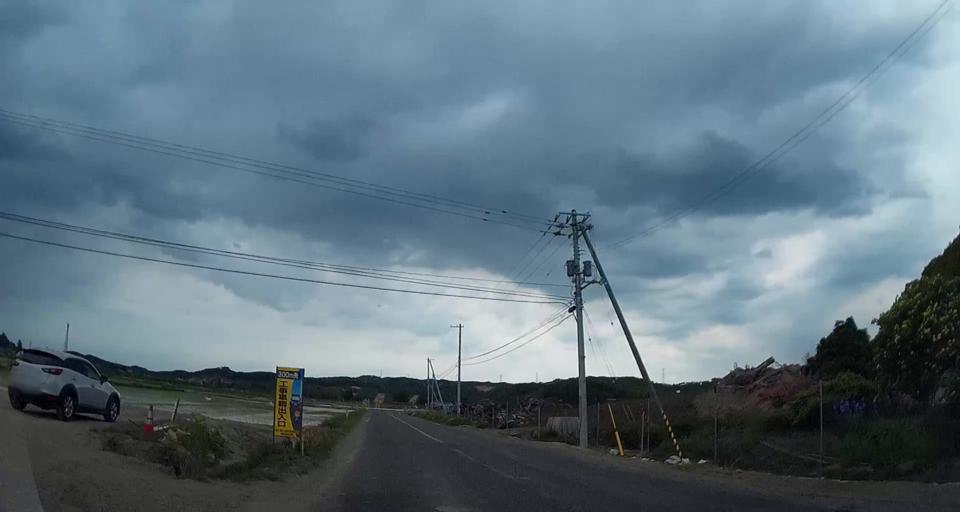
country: JP
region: Hokkaido
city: Chitose
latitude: 42.7553
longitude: 141.9367
